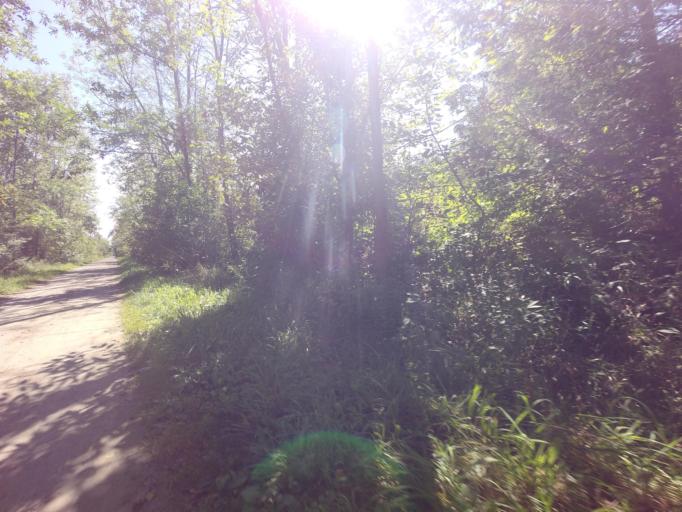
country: CA
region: Ontario
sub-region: Wellington County
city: Guelph
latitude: 43.6987
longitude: -80.3961
